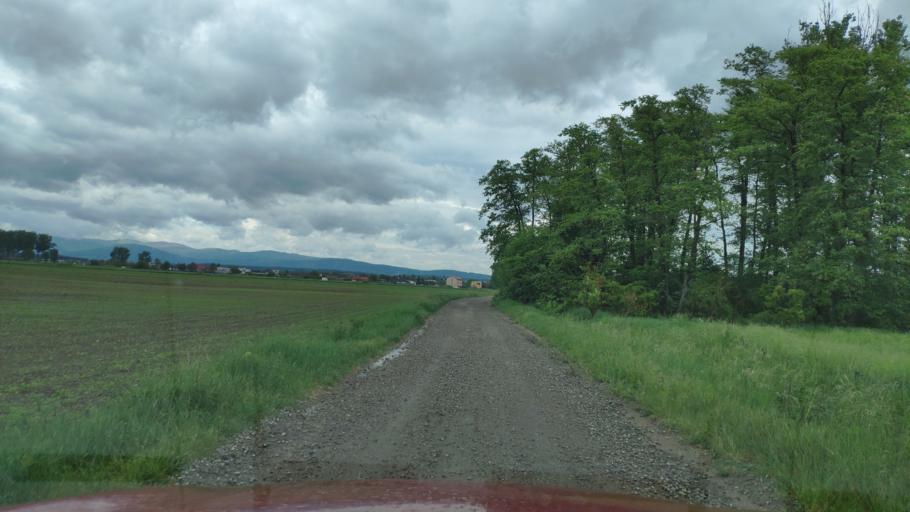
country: SK
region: Kosicky
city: Moldava nad Bodvou
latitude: 48.5637
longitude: 21.1210
